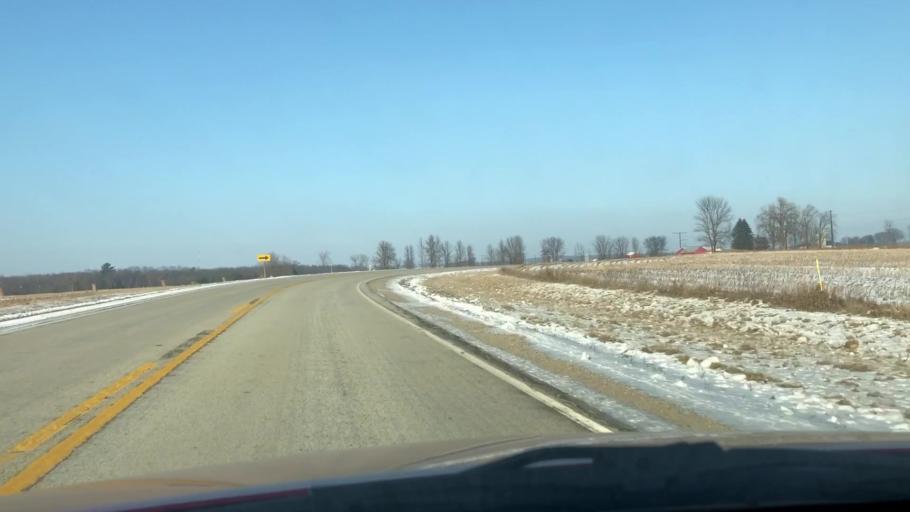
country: US
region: Wisconsin
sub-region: Outagamie County
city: Seymour
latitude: 44.4411
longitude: -88.3610
